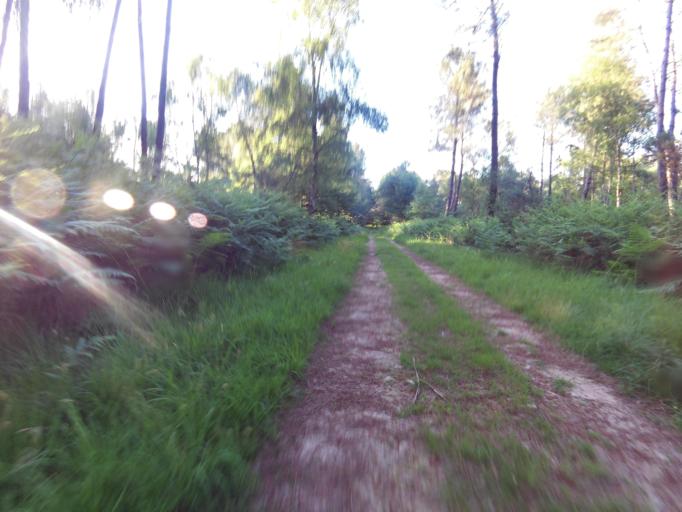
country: FR
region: Brittany
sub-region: Departement du Morbihan
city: Molac
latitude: 47.7479
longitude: -2.4145
